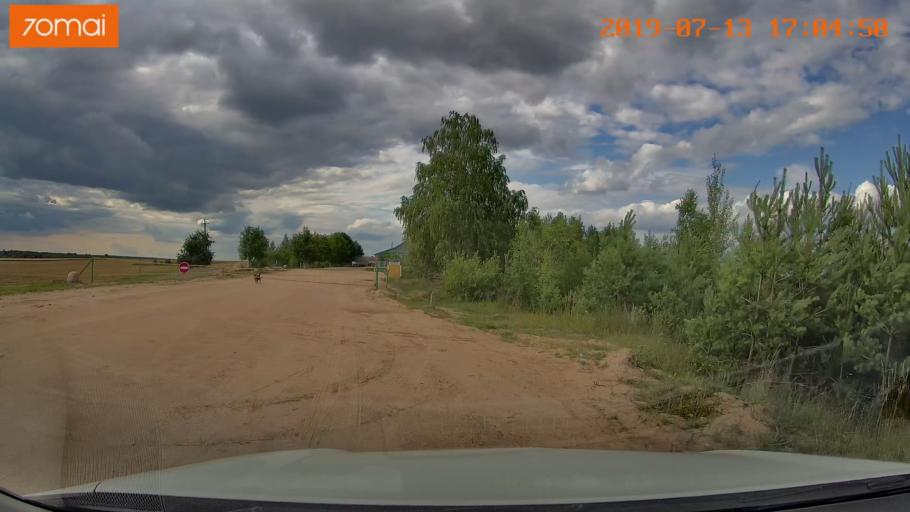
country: BY
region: Mogilev
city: Kirawsk
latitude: 53.2723
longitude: 29.3675
